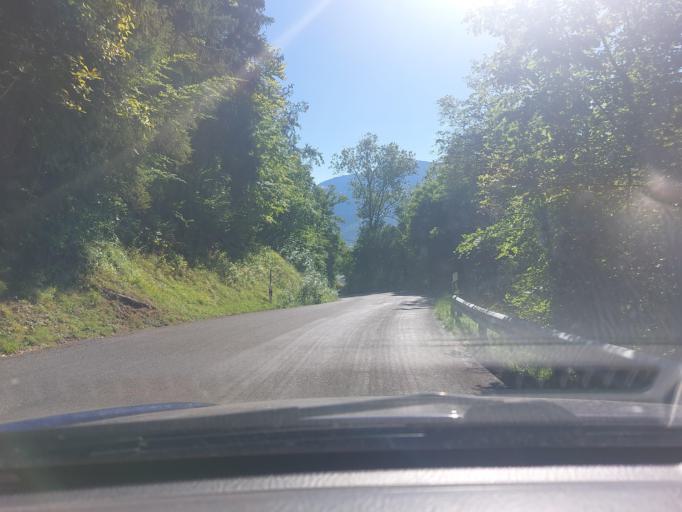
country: CH
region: Vaud
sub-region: Aigle District
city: Aigle
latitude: 46.3369
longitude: 6.9657
